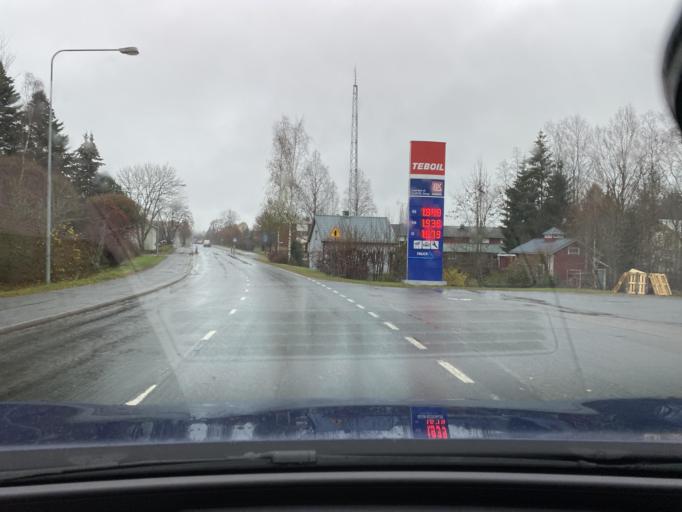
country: FI
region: Varsinais-Suomi
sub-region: Loimaa
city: Alastaro
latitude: 60.9492
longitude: 22.8652
